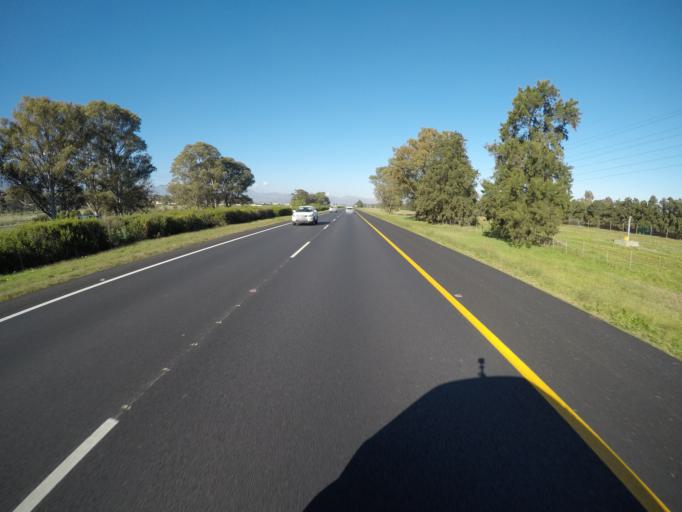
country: ZA
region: Western Cape
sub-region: Cape Winelands District Municipality
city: Stellenbosch
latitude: -34.0632
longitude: 18.8015
